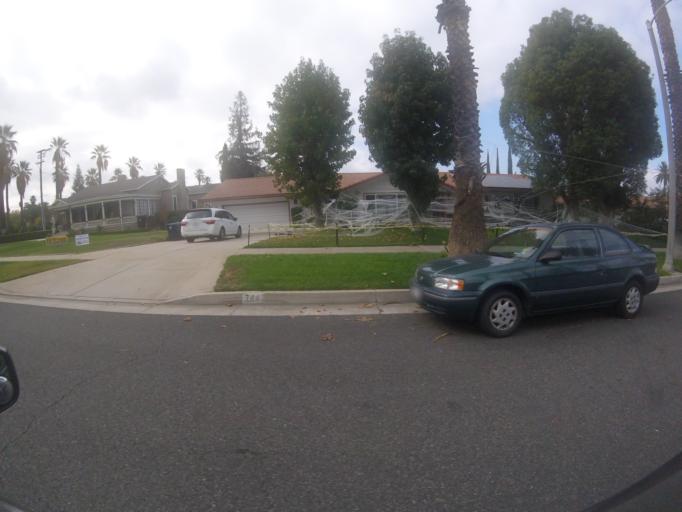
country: US
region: California
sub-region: San Bernardino County
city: Redlands
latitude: 34.0408
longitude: -117.1818
